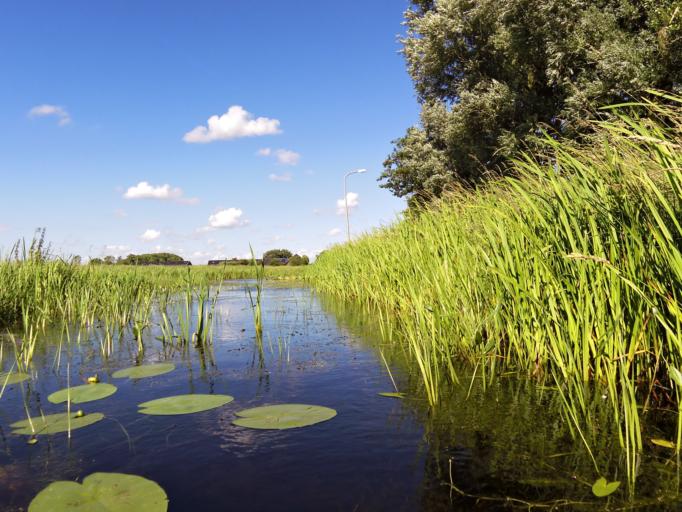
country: NL
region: South Holland
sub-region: Gemeente Wassenaar
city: Wassenaar
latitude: 52.1529
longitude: 4.4249
